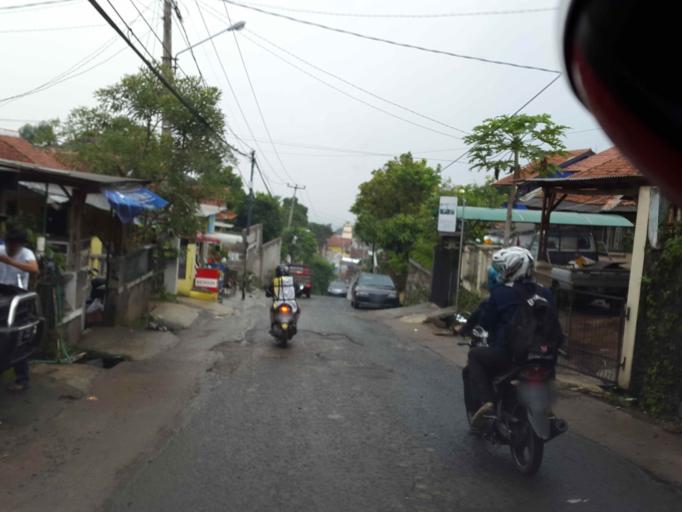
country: ID
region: West Java
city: Cimahi
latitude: -6.8509
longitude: 107.5812
